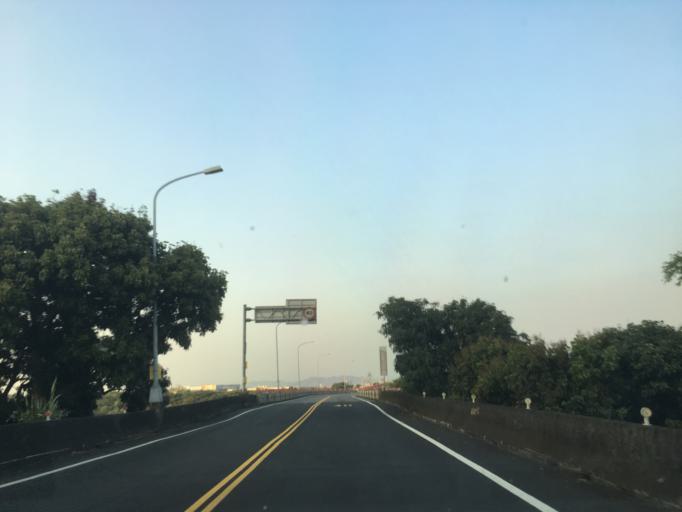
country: TW
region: Taiwan
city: Zhongxing New Village
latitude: 23.9517
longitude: 120.6568
